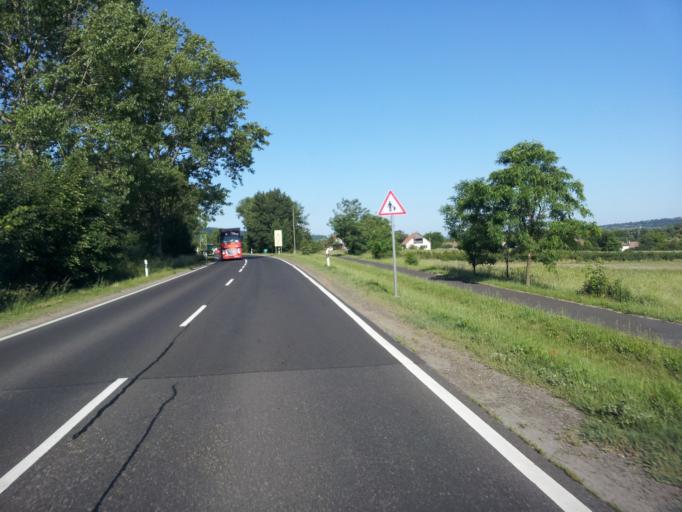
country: SK
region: Nitriansky
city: Sahy
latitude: 48.0531
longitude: 19.0083
